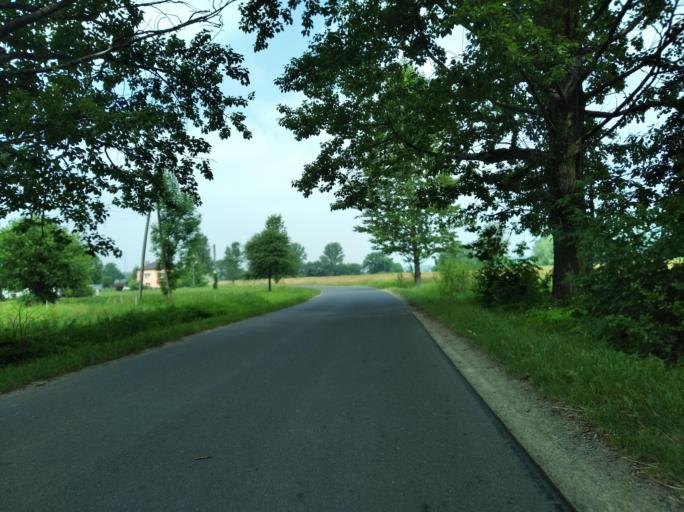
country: PL
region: Subcarpathian Voivodeship
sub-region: Powiat sanocki
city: Besko
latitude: 49.6247
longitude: 21.9346
